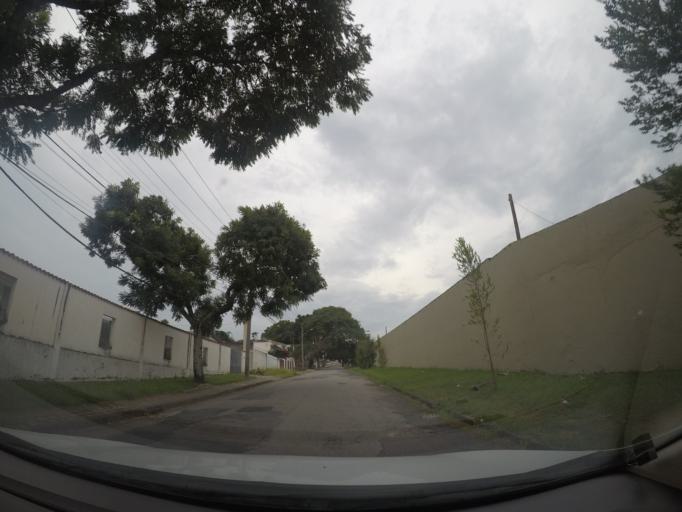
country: BR
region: Parana
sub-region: Curitiba
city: Curitiba
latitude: -25.4648
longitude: -49.2451
